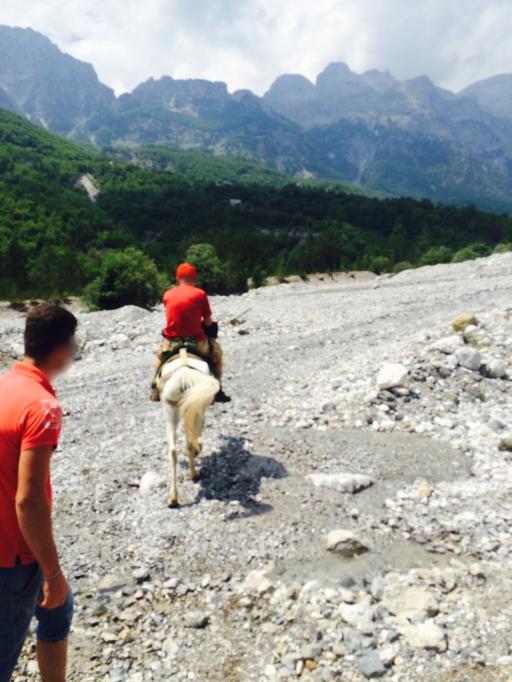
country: AL
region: Shkoder
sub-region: Rrethi i Shkodres
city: Nicaj-Shale
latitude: 42.3977
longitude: 19.7721
